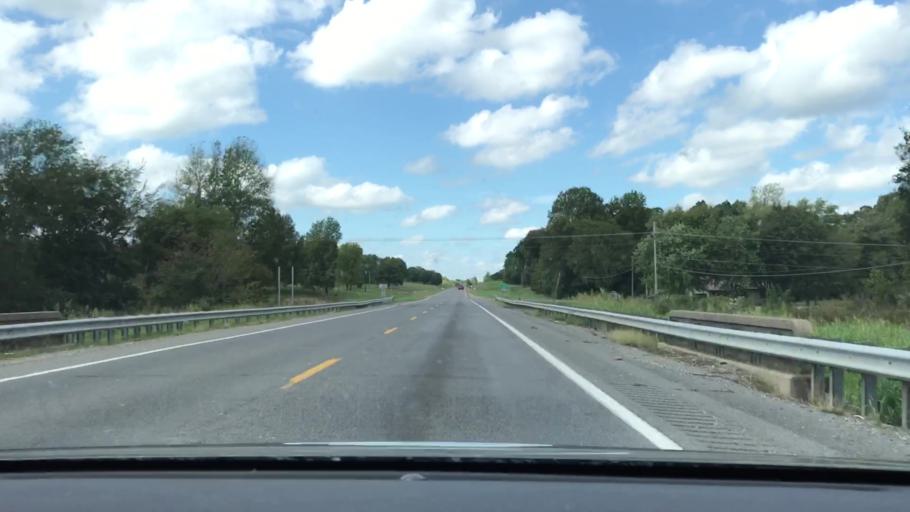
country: US
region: Kentucky
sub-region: Livingston County
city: Ledbetter
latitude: 37.0076
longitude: -88.4828
